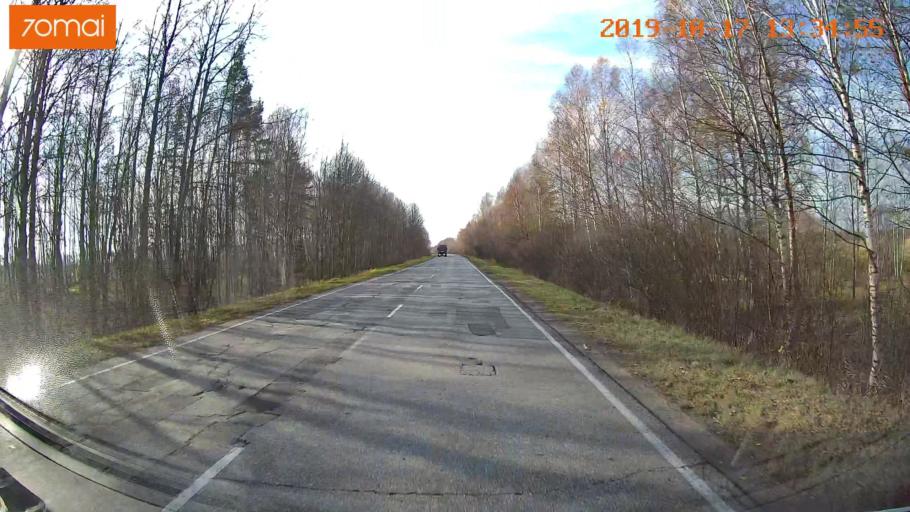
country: RU
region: Vladimir
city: Velikodvorskiy
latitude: 55.1438
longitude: 40.7031
